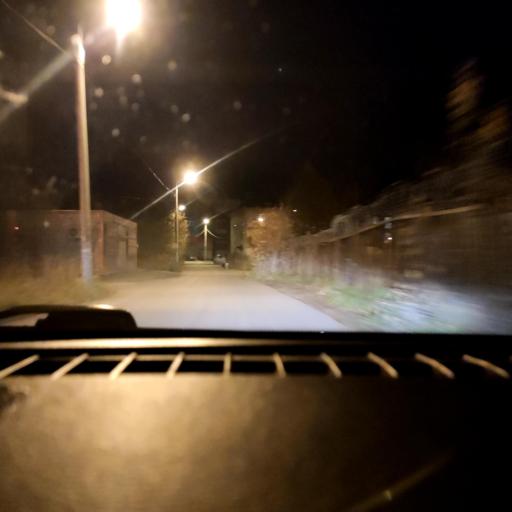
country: RU
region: Perm
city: Perm
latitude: 58.0368
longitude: 56.3567
